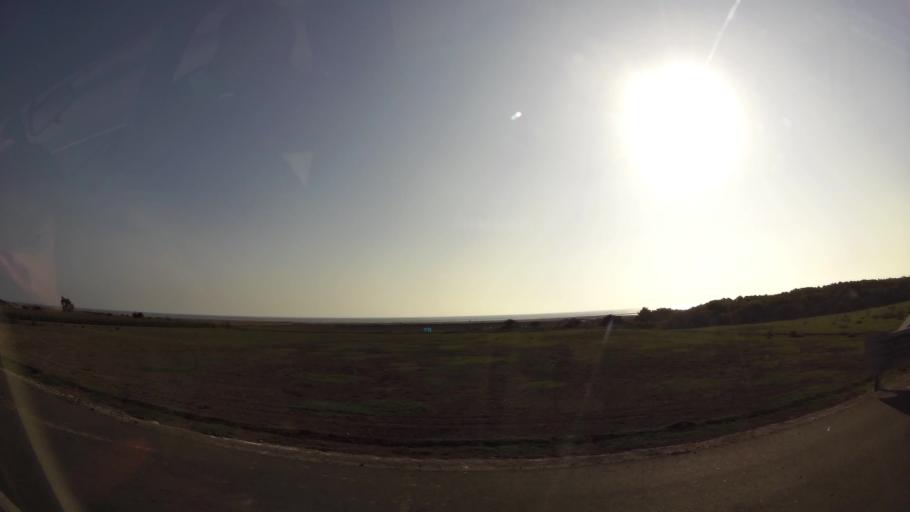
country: PE
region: Ica
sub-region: Provincia de Chincha
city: Chincha Baja
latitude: -13.5302
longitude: -76.1832
